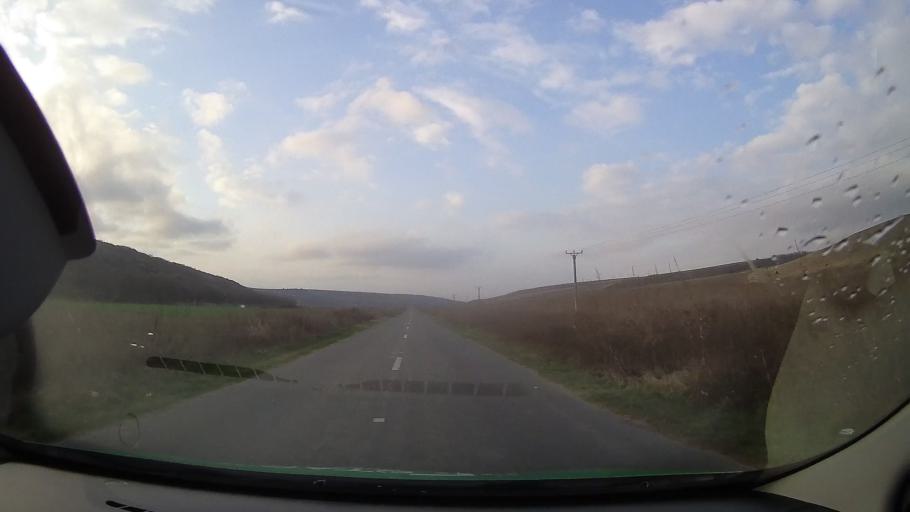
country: RO
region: Constanta
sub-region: Comuna Dobromir
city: Dobromir
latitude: 44.0304
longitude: 27.8596
